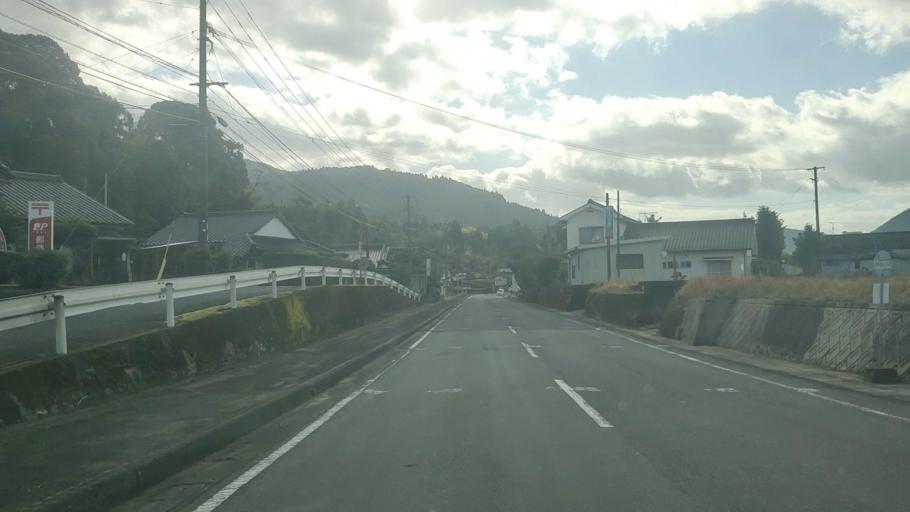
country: JP
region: Kagoshima
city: Okuchi-shinohara
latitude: 31.9931
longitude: 130.7481
